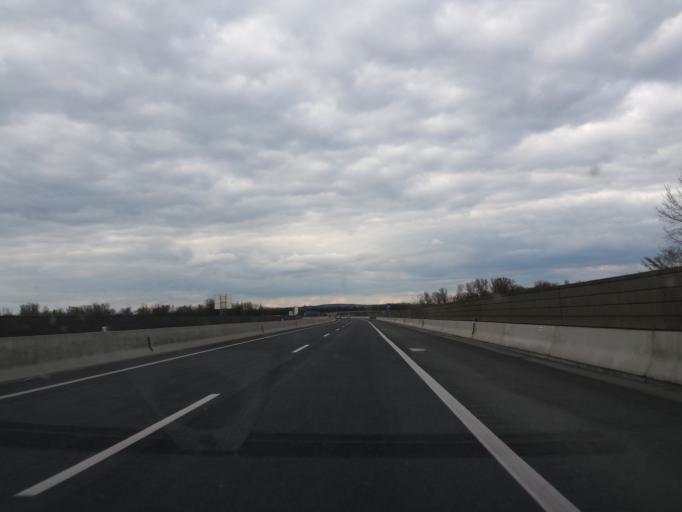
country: AT
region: Lower Austria
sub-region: Politischer Bezirk Krems
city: Grafenegg
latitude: 48.3991
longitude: 15.7359
